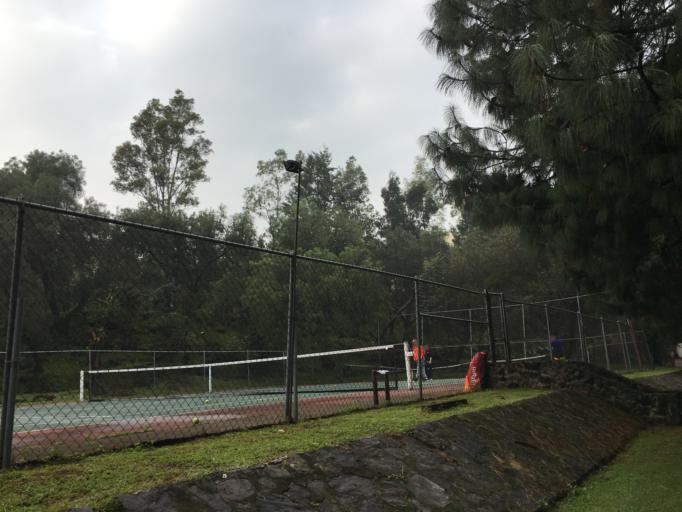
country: MX
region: Mexico City
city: Tlalpan
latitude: 19.2818
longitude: -99.1464
